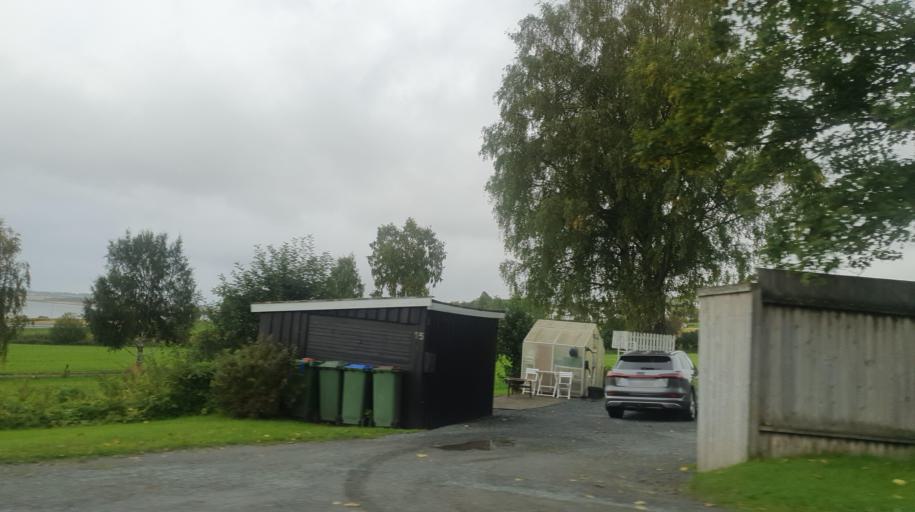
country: NO
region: Nord-Trondelag
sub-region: Levanger
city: Skogn
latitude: 63.7086
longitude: 11.1909
